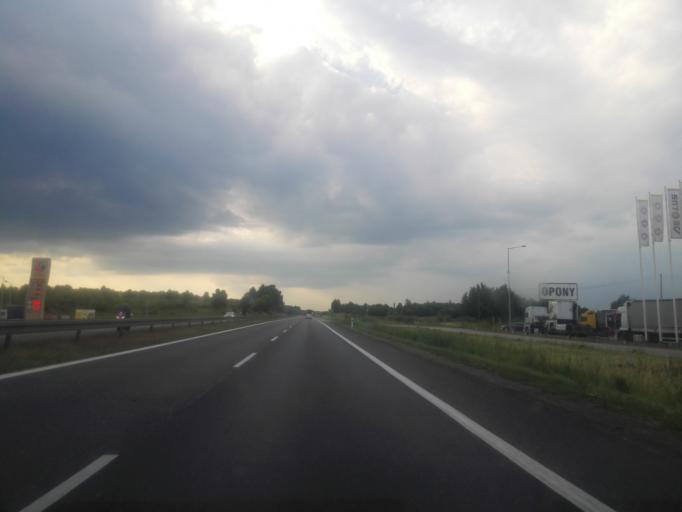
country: PL
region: Silesian Voivodeship
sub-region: Powiat myszkowski
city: Kozieglowy
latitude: 50.6219
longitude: 19.1458
